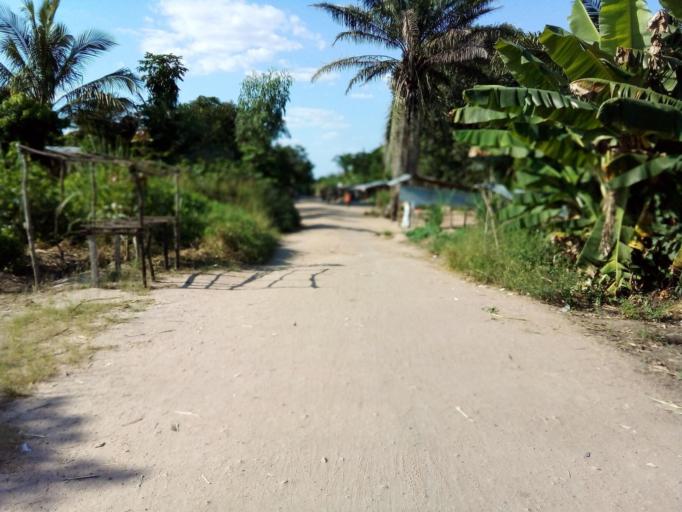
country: MZ
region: Zambezia
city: Quelimane
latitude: -17.5976
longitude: 36.8279
